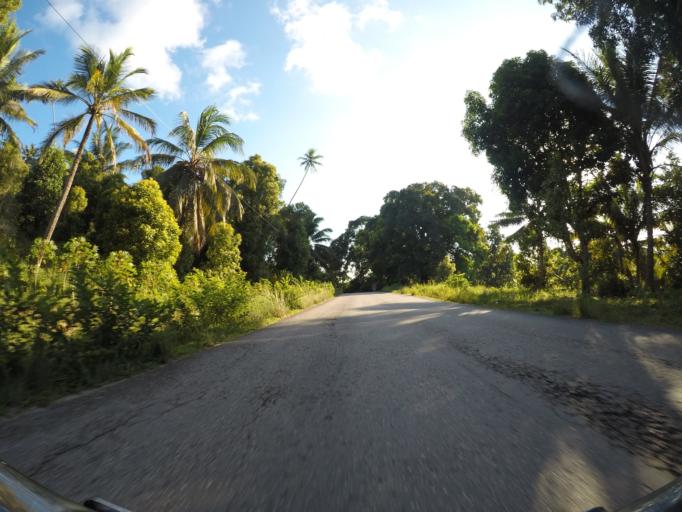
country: TZ
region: Pemba South
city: Mtambile
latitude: -5.3647
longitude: 39.7112
